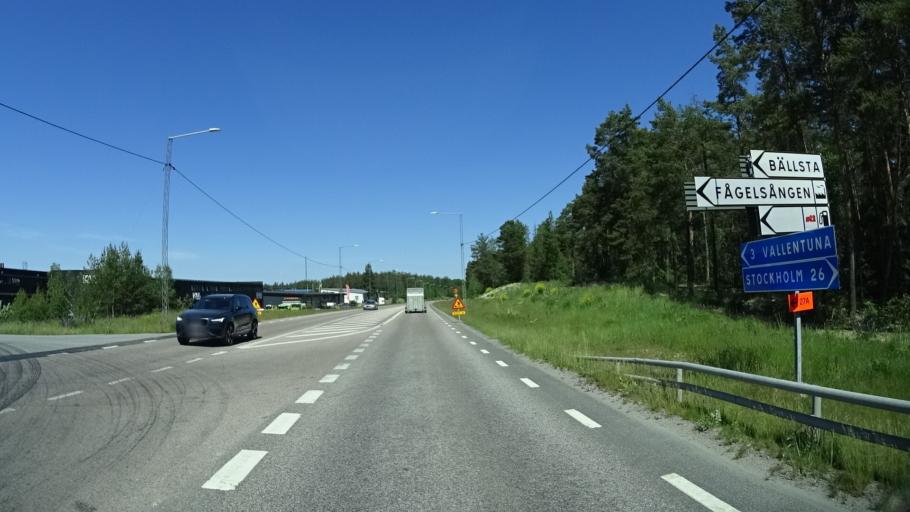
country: SE
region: Stockholm
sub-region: Vallentuna Kommun
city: Vallentuna
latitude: 59.5134
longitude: 18.0952
